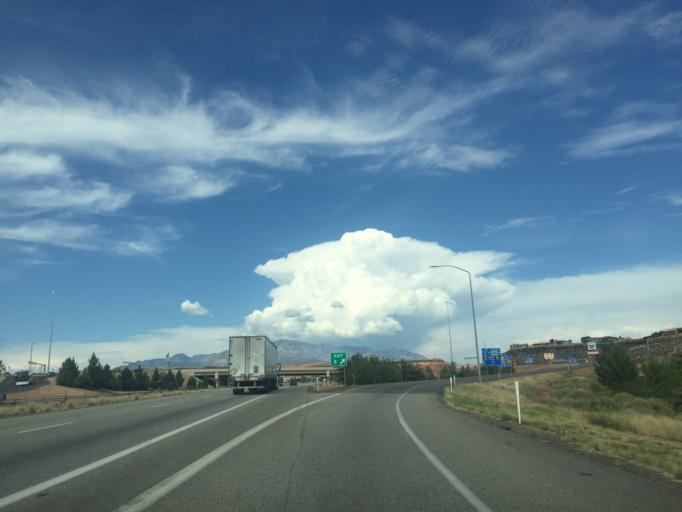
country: US
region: Utah
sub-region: Washington County
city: Saint George
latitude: 37.1070
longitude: -113.5589
